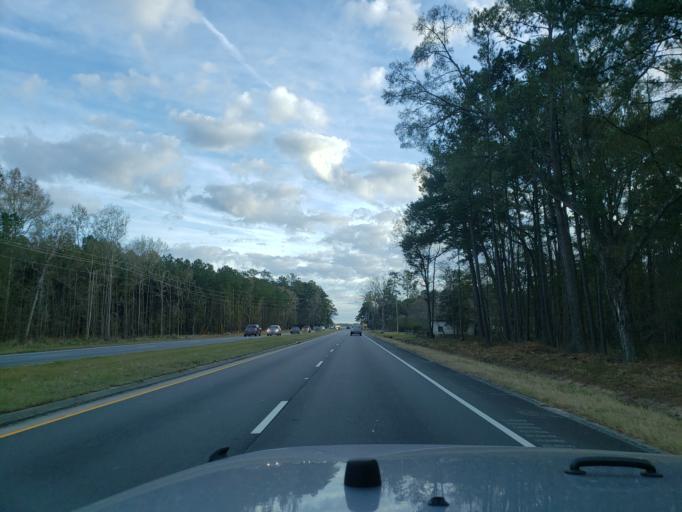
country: US
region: Georgia
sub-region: Chatham County
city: Port Wentworth
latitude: 32.2054
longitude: -81.2003
